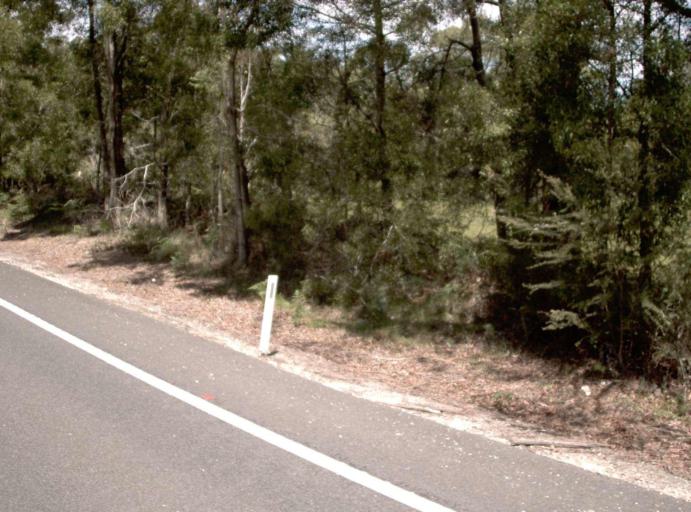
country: AU
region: New South Wales
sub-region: Bombala
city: Bombala
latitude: -37.5654
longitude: 149.0806
